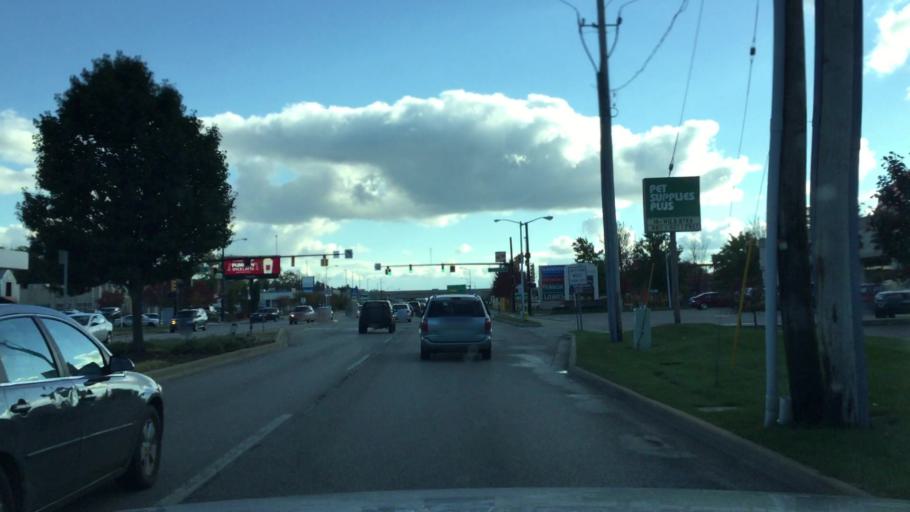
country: US
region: Michigan
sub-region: Kalamazoo County
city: Portage
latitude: 42.2414
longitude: -85.5896
